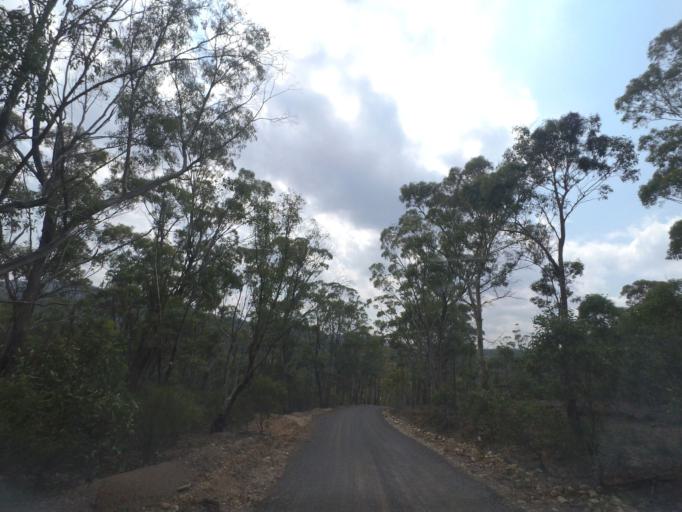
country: AU
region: Victoria
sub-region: Moorabool
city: Bacchus Marsh
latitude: -37.5953
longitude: 144.4333
